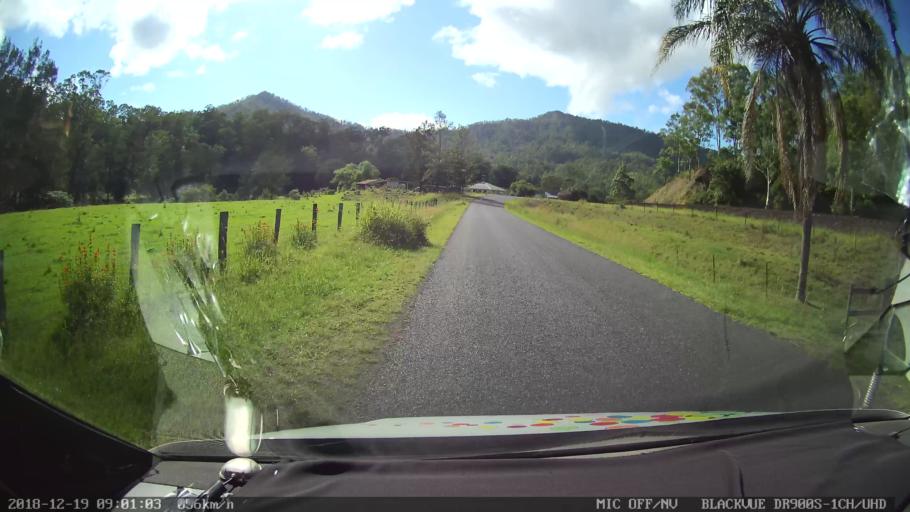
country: AU
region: New South Wales
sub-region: Kyogle
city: Kyogle
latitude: -28.4362
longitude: 152.9582
